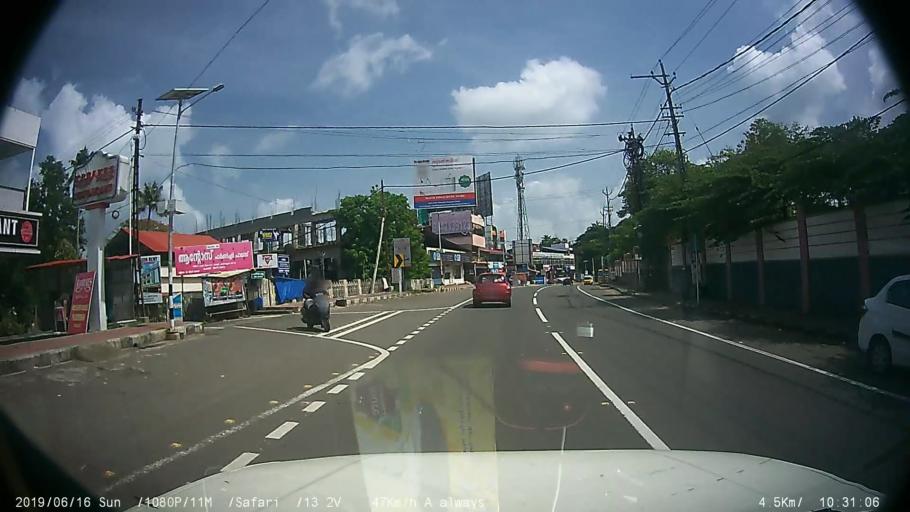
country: IN
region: Kerala
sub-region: Kottayam
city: Changanacheri
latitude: 9.4499
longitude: 76.5379
